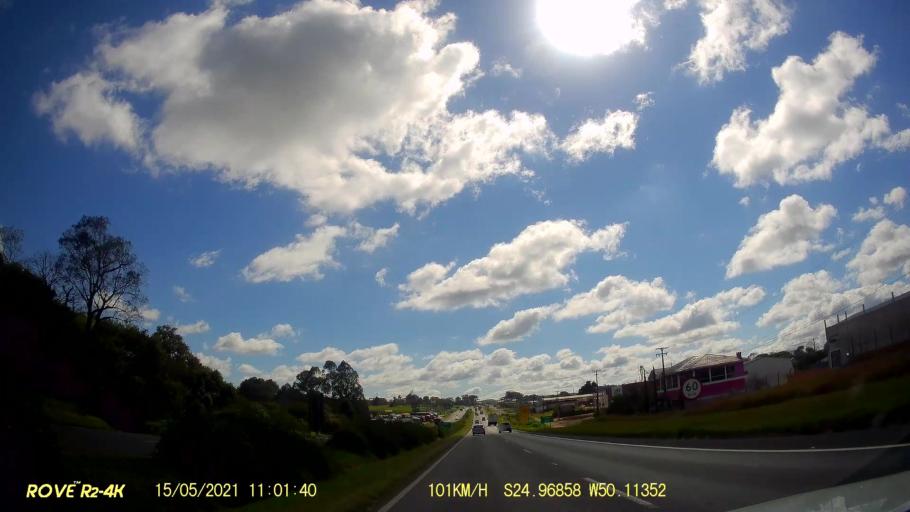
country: BR
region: Parana
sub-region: Carambei
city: Carambei
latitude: -24.9687
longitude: -50.1134
